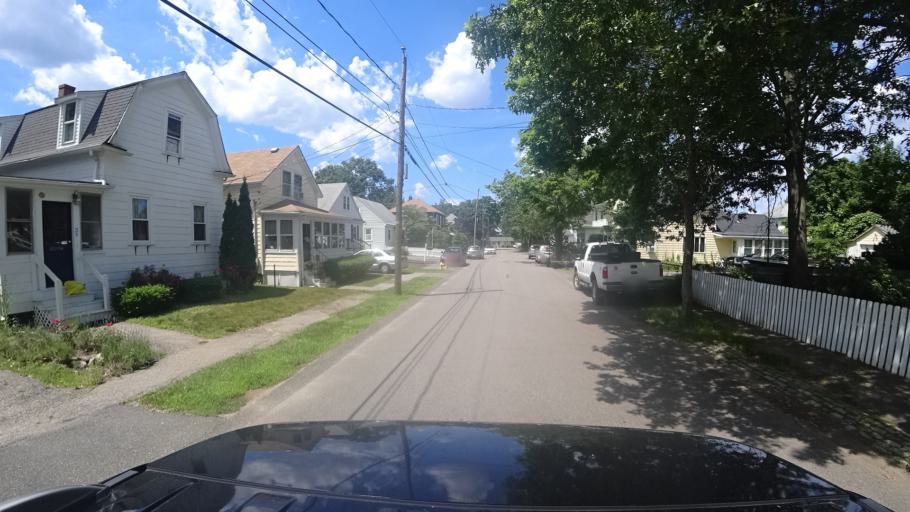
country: US
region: Massachusetts
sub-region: Norfolk County
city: Dedham
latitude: 42.2739
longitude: -71.1795
